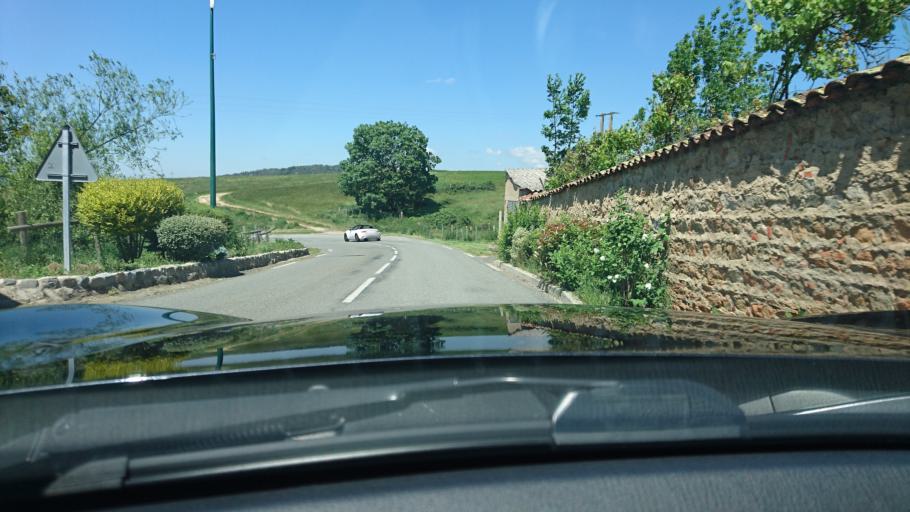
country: FR
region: Rhone-Alpes
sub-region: Departement de la Loire
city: Rozier-en-Donzy
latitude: 45.7936
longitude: 4.2960
